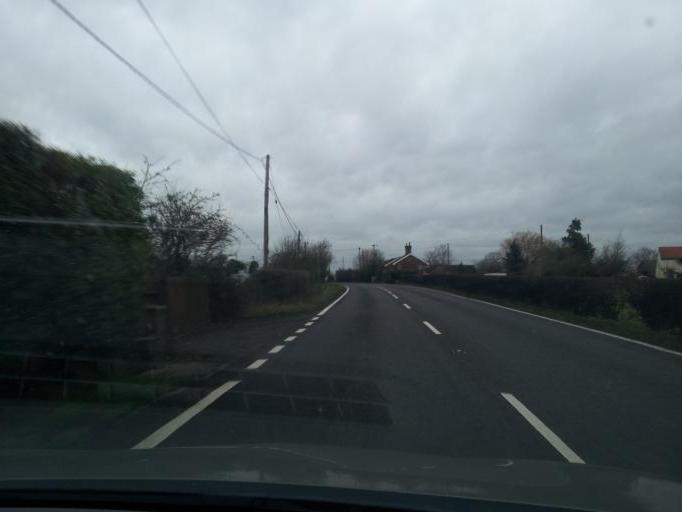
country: GB
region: England
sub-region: Suffolk
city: Botesdale
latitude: 52.3291
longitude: 0.9320
